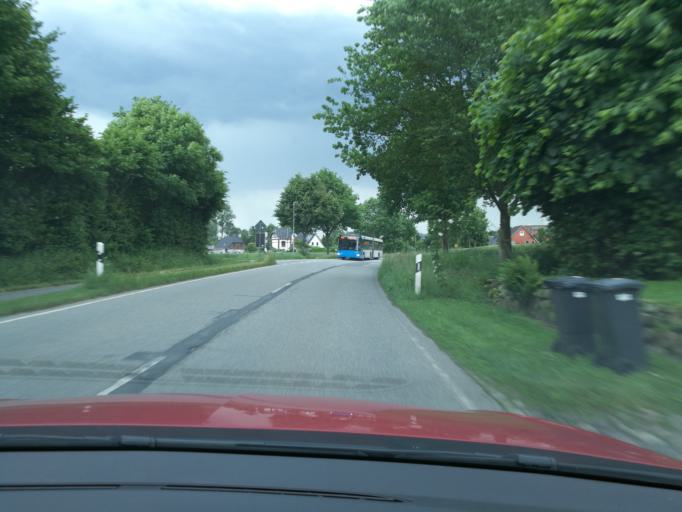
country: DE
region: Schleswig-Holstein
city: Lasbek
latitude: 53.7405
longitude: 10.3669
